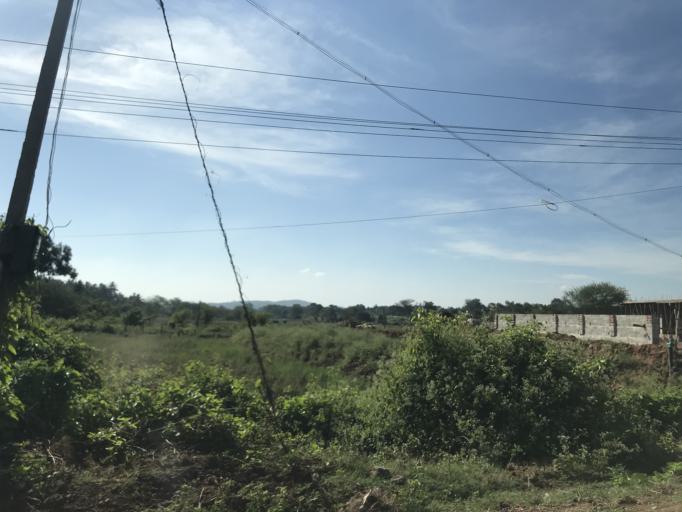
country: IN
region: Karnataka
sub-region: Mysore
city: Sargur
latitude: 12.1222
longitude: 76.4865
